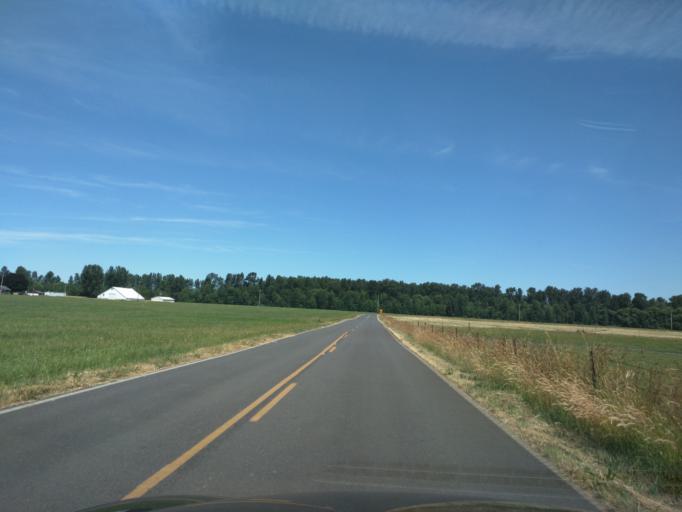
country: US
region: Washington
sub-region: Whatcom County
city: Lynden
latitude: 48.9321
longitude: -122.4195
